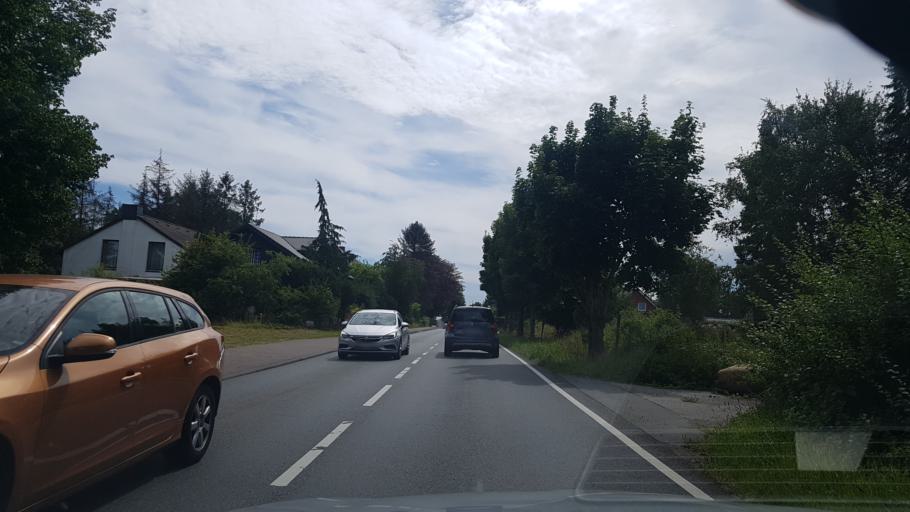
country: DE
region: Schleswig-Holstein
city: Gross Buchwald
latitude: 54.1634
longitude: 10.0797
